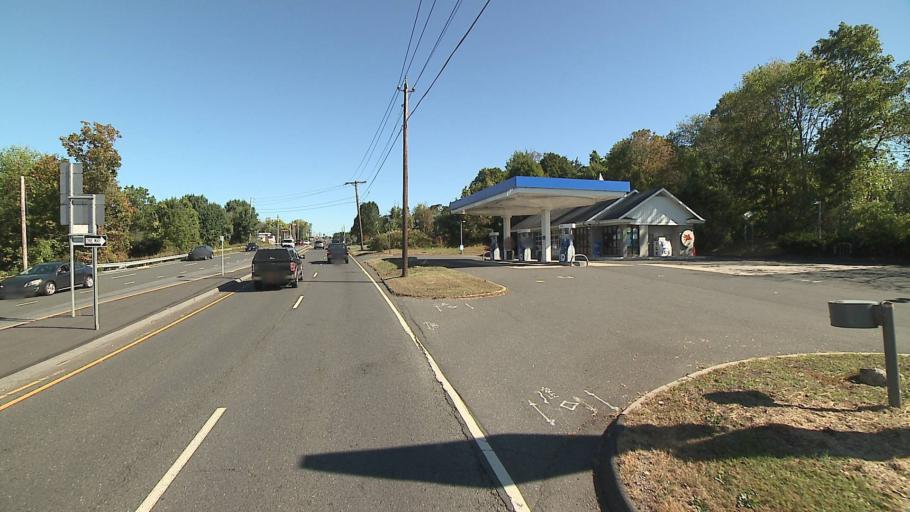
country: US
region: Connecticut
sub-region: Fairfield County
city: Danbury
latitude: 41.4344
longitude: -73.4101
